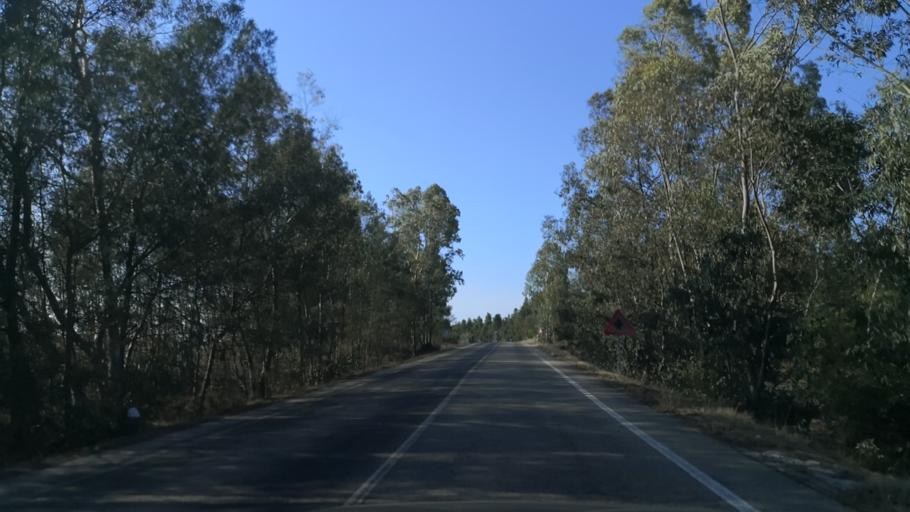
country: PT
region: Santarem
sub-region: Almeirim
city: Fazendas de Almeirim
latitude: 39.0963
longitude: -8.5755
